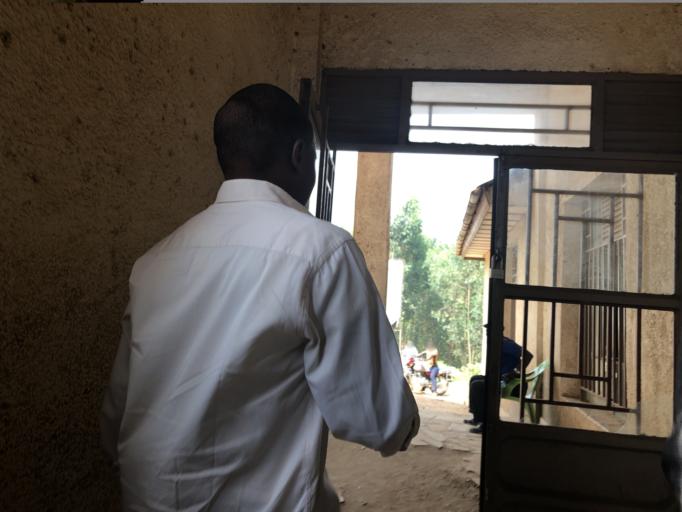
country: UG
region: Western Region
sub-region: Kasese District
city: Kilembe
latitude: 0.0395
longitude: 29.7194
